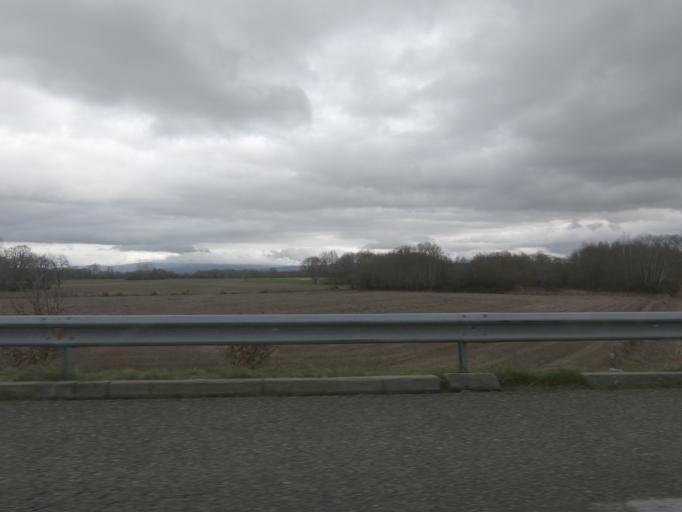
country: ES
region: Galicia
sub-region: Provincia de Ourense
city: Xinzo de Limia
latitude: 42.1263
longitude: -7.7401
